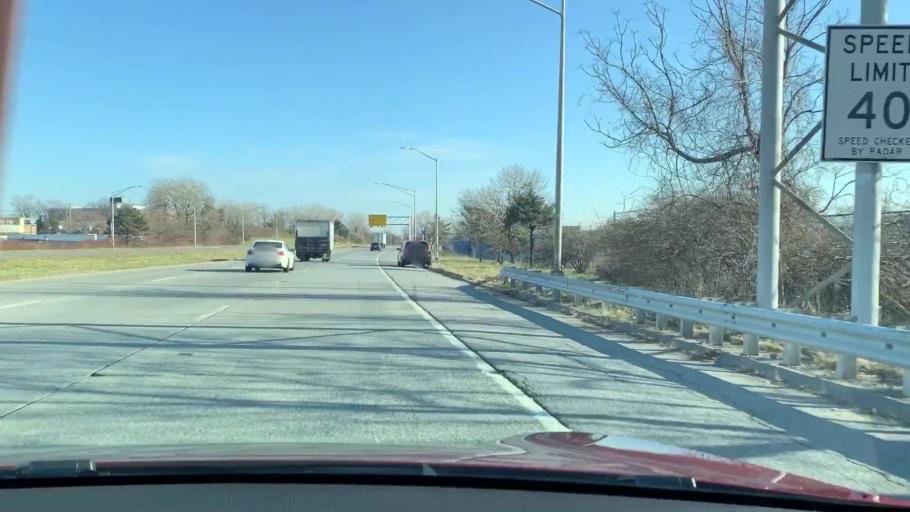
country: US
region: New York
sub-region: Queens County
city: Jamaica
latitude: 40.6634
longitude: -73.7846
